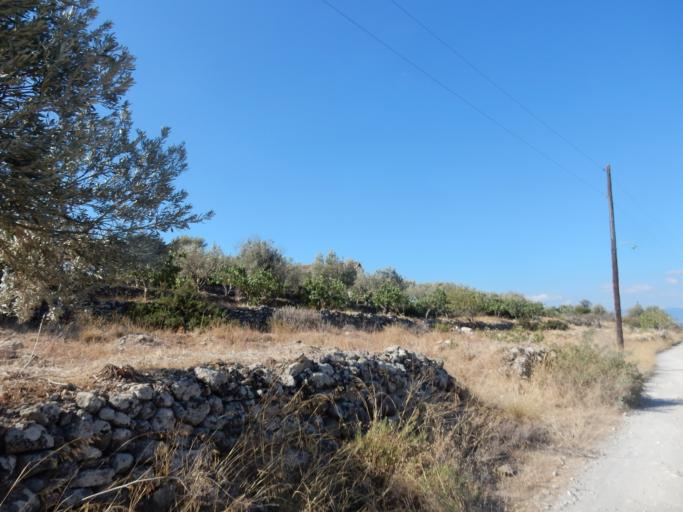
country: GR
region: Attica
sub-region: Nomos Piraios
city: Kypseli
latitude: 37.7330
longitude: 23.4547
